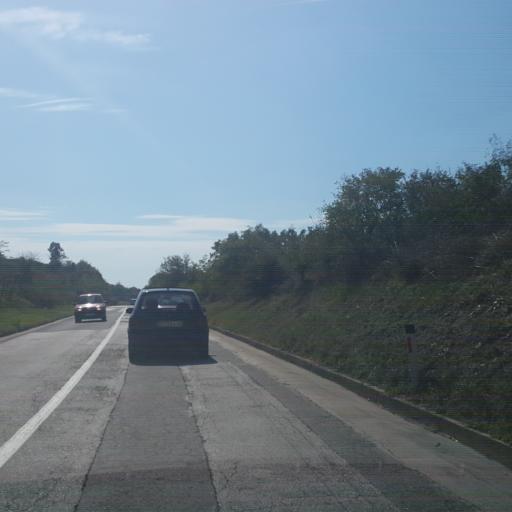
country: RS
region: Central Serbia
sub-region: Zajecarski Okrug
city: Zajecar
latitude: 43.7604
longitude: 22.3095
